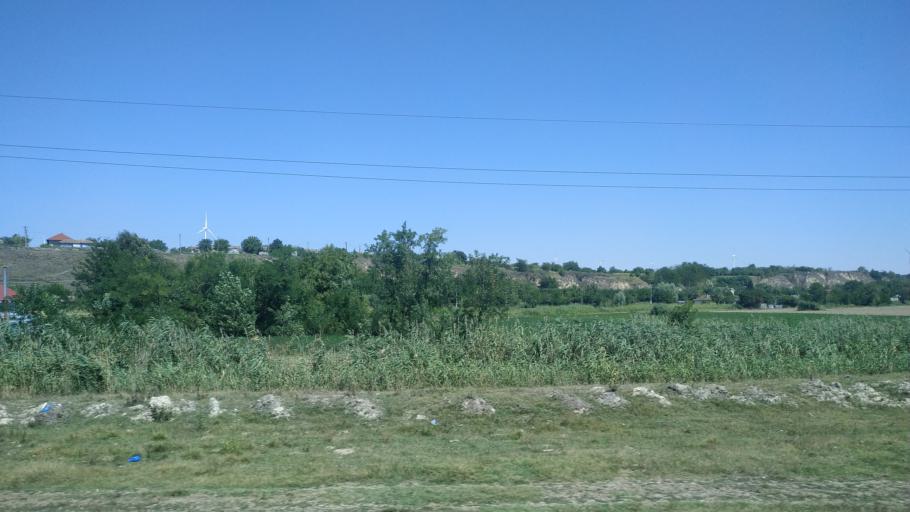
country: RO
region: Constanta
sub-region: Comuna Saligny
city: Saligny
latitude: 44.2752
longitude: 28.0914
